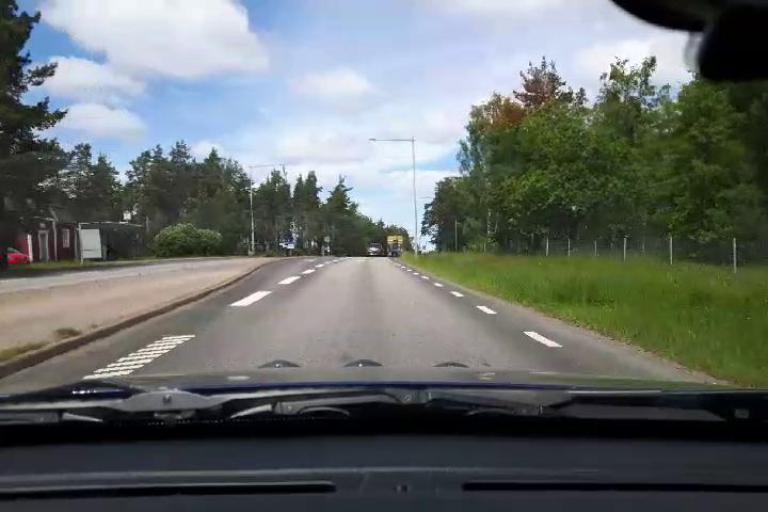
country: SE
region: Uppsala
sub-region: Osthammars Kommun
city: Bjorklinge
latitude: 60.0312
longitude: 17.5524
